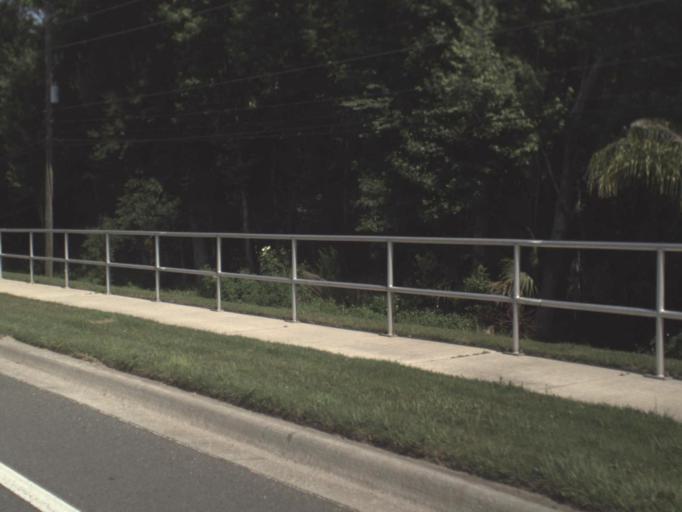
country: US
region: Florida
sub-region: Duval County
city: Neptune Beach
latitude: 30.2874
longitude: -81.4926
